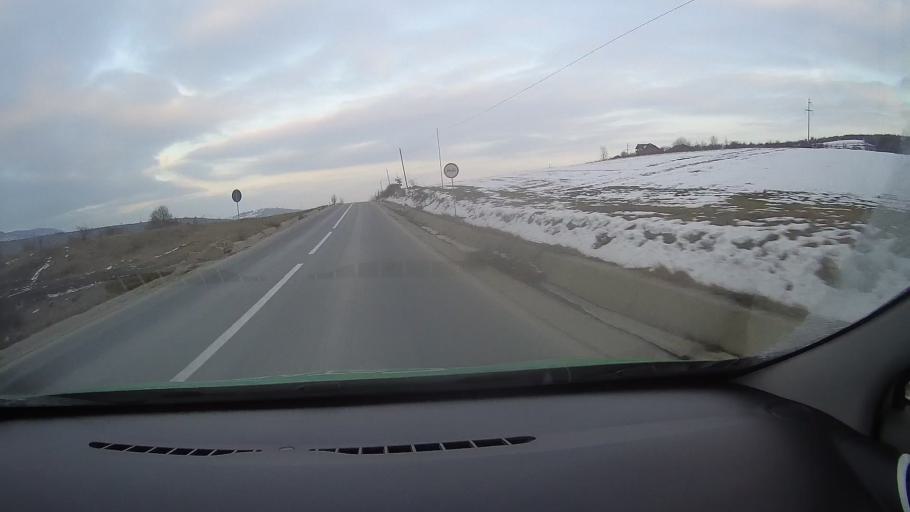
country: RO
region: Harghita
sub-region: Comuna Lupeni
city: Lupeni
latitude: 46.3570
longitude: 25.2032
